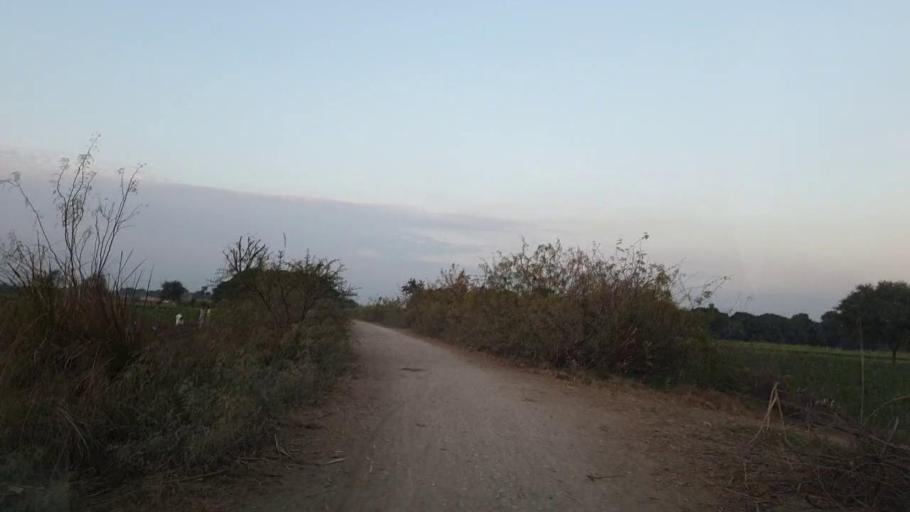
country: PK
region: Sindh
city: Tando Jam
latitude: 25.5013
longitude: 68.5852
